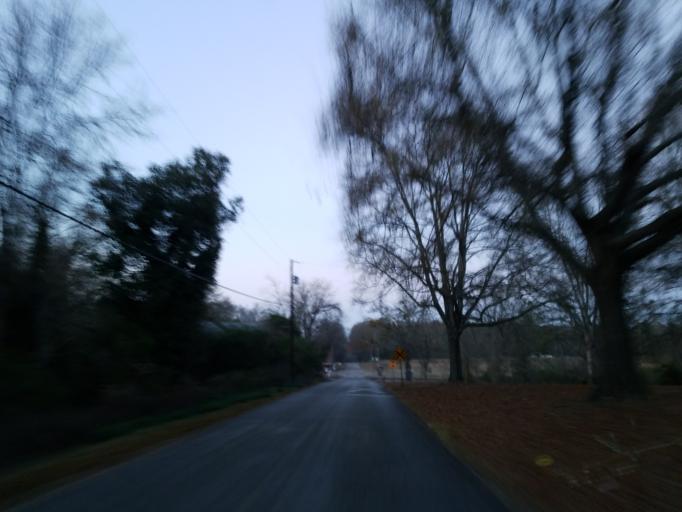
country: US
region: Alabama
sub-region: Sumter County
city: York
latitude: 32.4225
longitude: -88.4382
